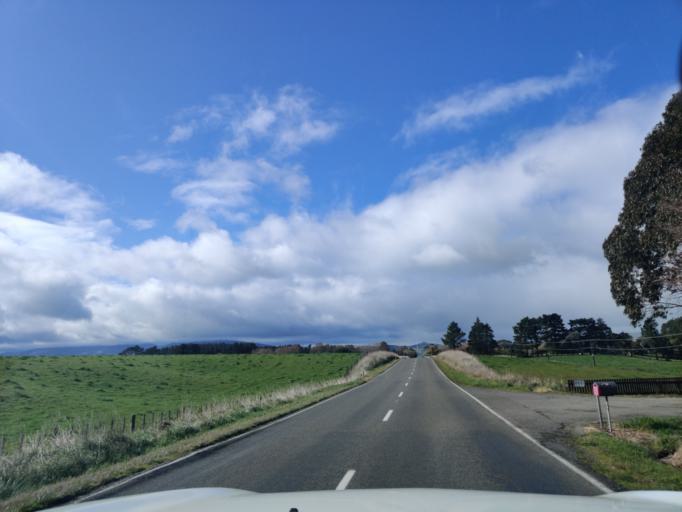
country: NZ
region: Manawatu-Wanganui
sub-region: Palmerston North City
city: Palmerston North
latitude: -40.2886
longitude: 175.6993
